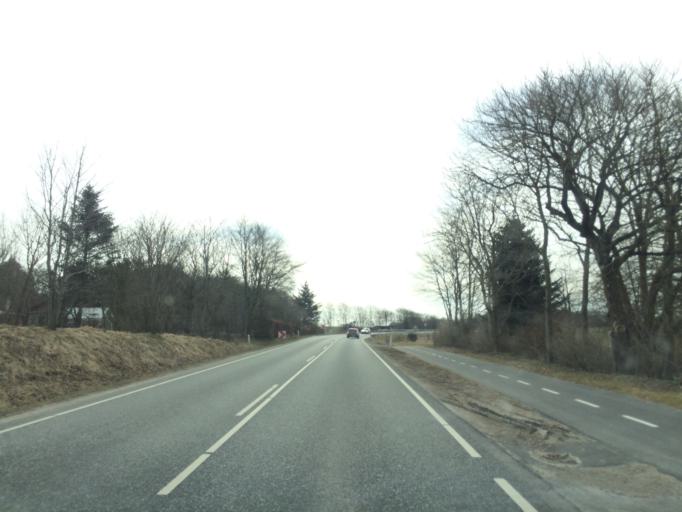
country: DK
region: Central Jutland
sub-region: Ringkobing-Skjern Kommune
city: Videbaek
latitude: 56.1086
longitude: 8.5061
